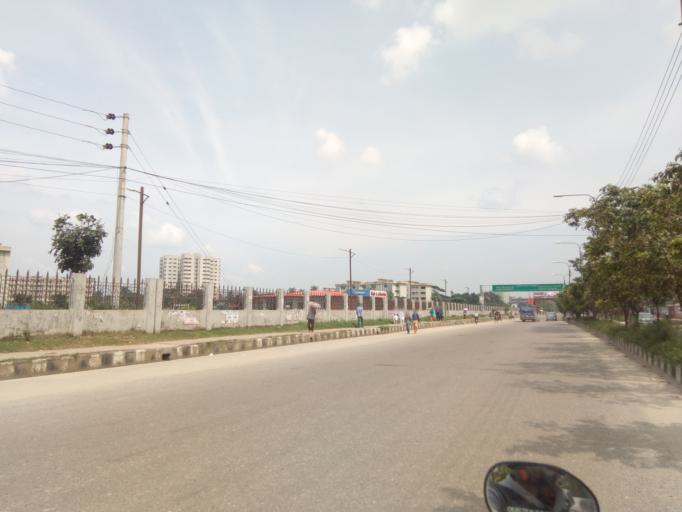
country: BD
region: Dhaka
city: Tungi
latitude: 23.8220
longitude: 90.3939
